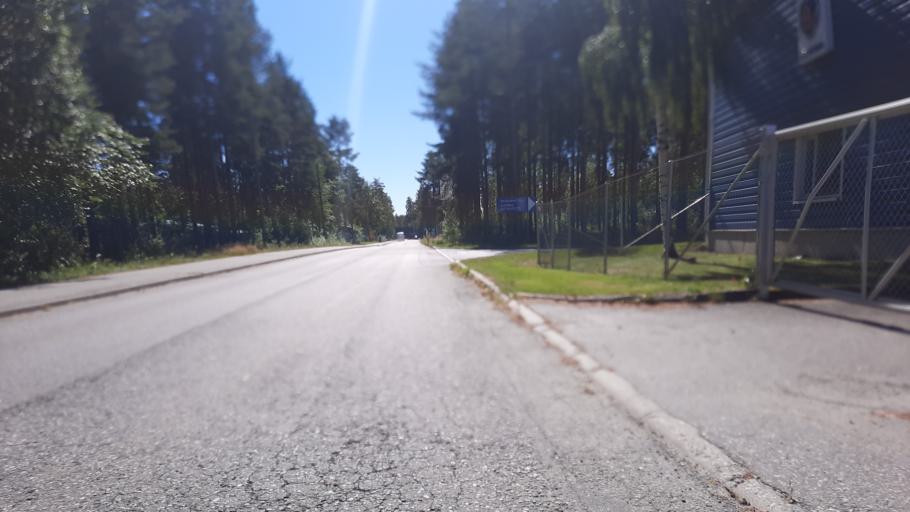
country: FI
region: North Karelia
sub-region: Joensuu
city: Joensuu
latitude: 62.6213
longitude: 29.7432
